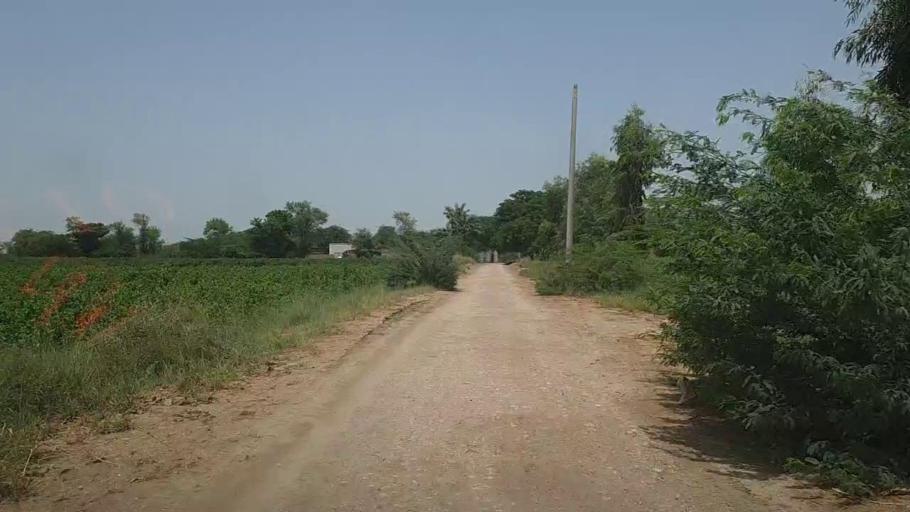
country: PK
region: Sindh
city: Pad Idan
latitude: 26.8478
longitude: 68.2964
